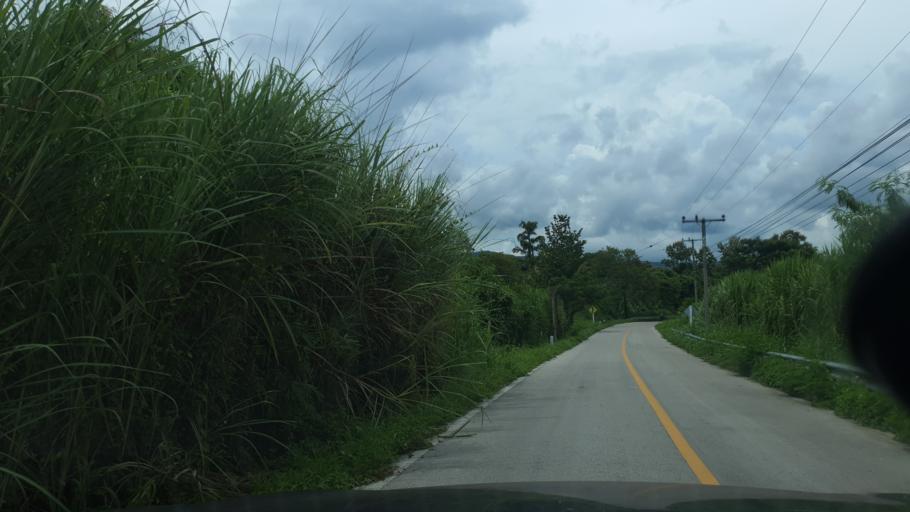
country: TH
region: Lampang
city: Hang Chat
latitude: 18.3958
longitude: 99.2646
